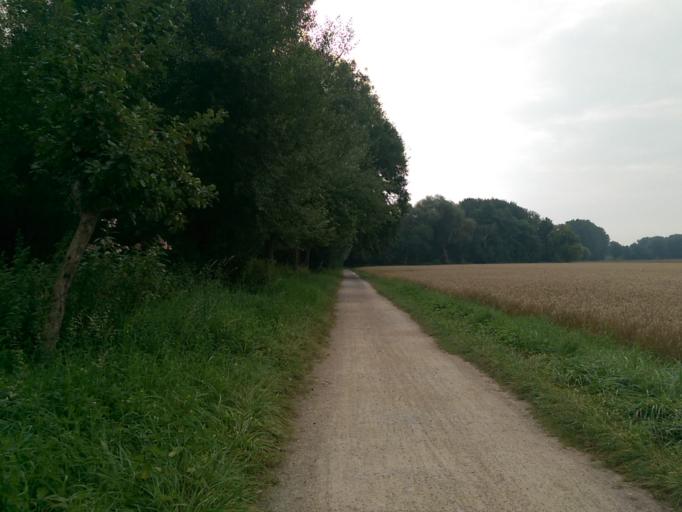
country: DE
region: North Rhine-Westphalia
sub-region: Regierungsbezirk Detmold
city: Guetersloh
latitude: 51.9453
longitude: 8.3232
